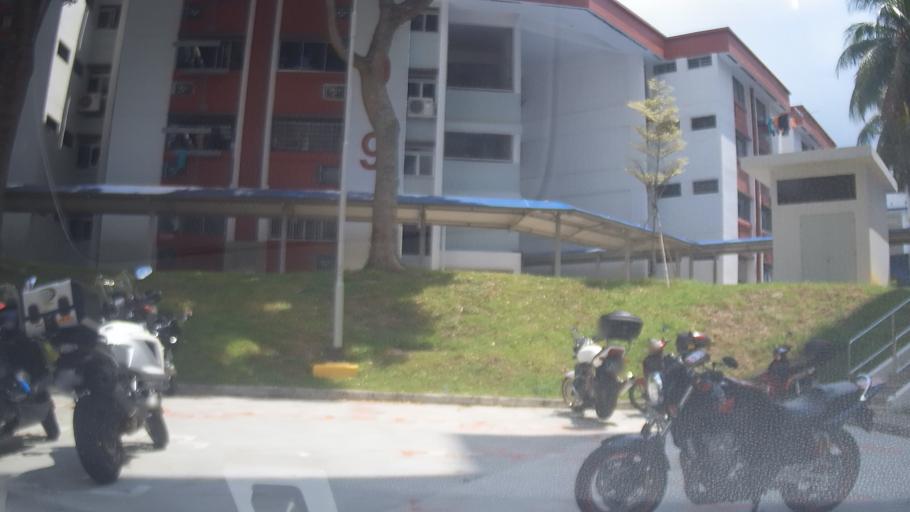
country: MY
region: Johor
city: Johor Bahru
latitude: 1.4373
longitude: 103.7813
